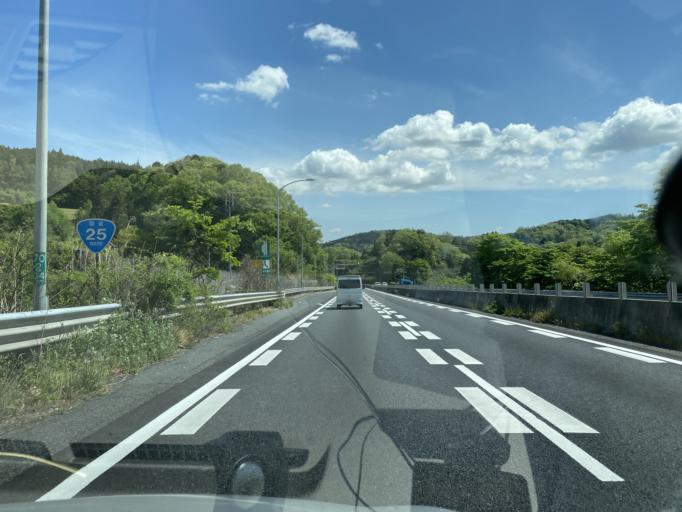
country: JP
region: Mie
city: Nabari
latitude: 34.6549
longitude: 136.0296
